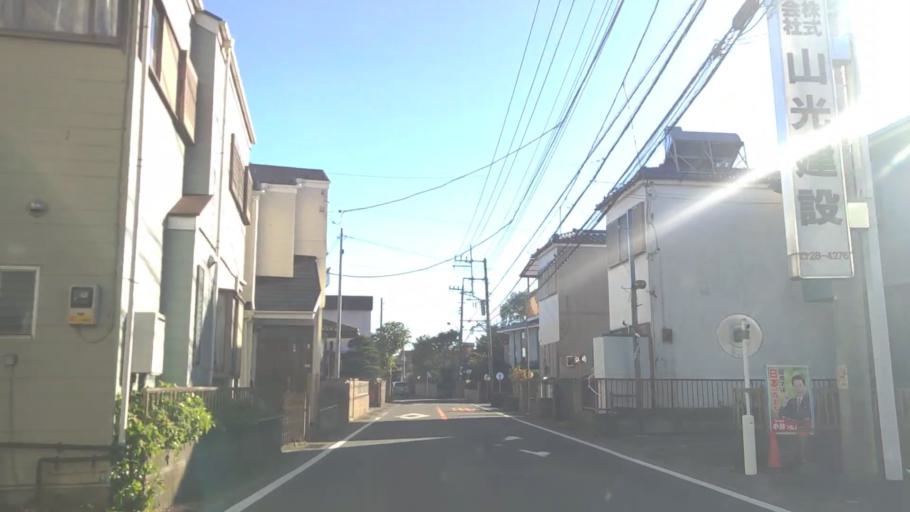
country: JP
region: Kanagawa
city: Atsugi
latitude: 35.4178
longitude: 139.3655
